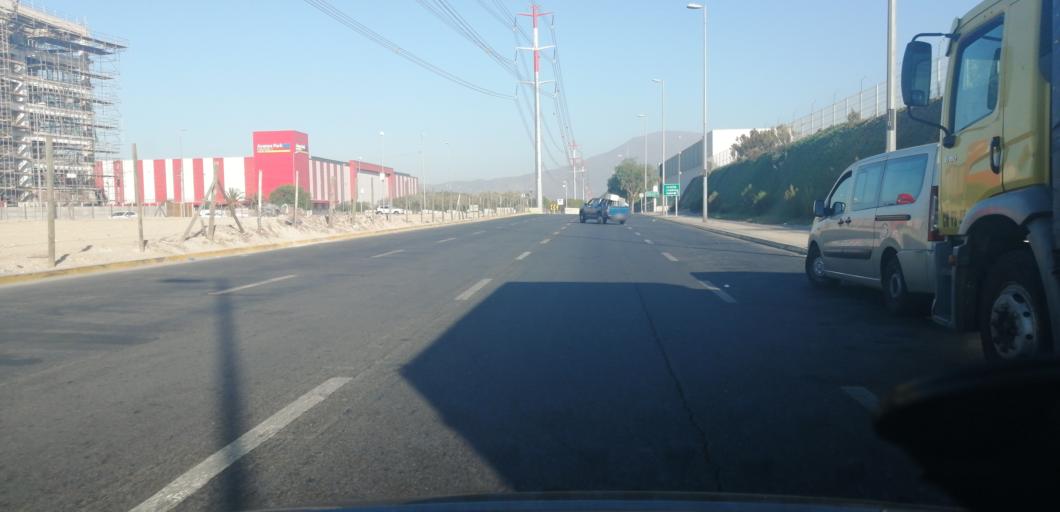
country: CL
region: Santiago Metropolitan
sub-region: Provincia de Santiago
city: Lo Prado
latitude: -33.4320
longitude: -70.7868
